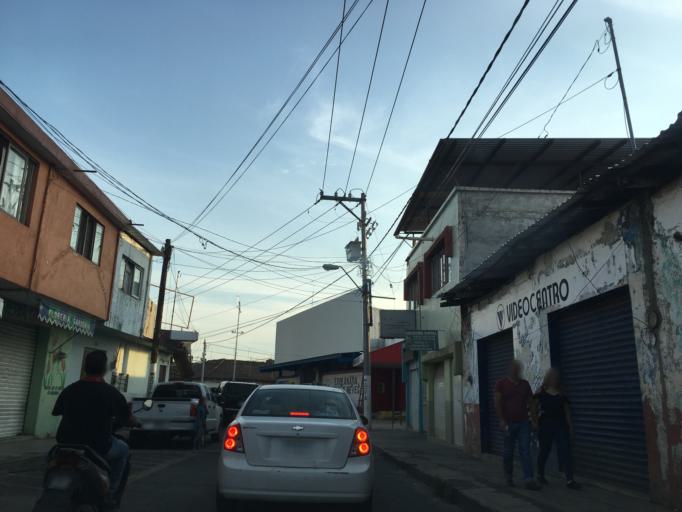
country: MX
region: Michoacan
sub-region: Los Reyes
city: La Higuerita (Colonia San Rafael)
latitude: 19.5878
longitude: -102.4755
